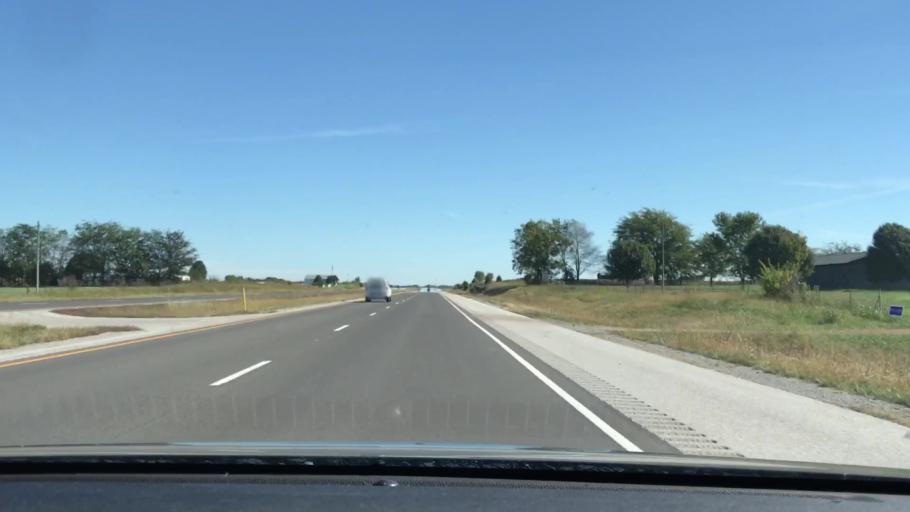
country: US
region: Kentucky
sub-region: Logan County
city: Russellville
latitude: 36.8219
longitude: -86.9931
